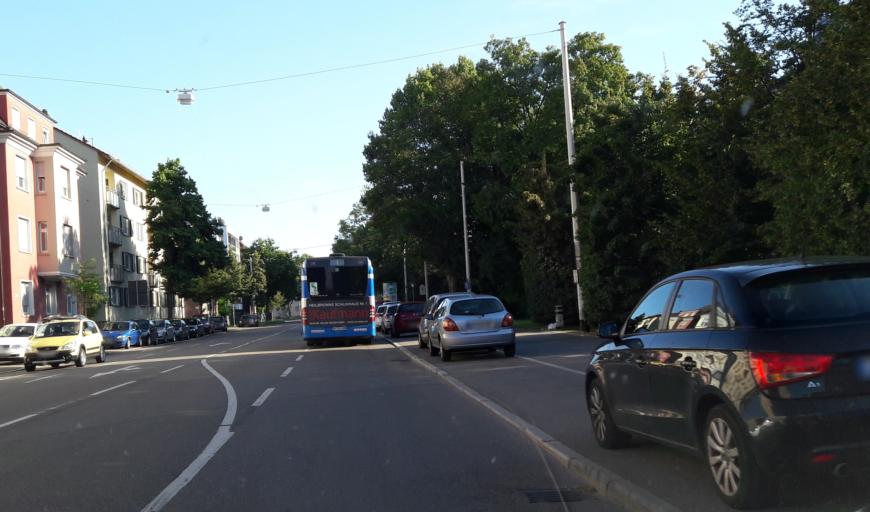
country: DE
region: Baden-Wuerttemberg
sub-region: Regierungsbezirk Stuttgart
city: Heilbronn
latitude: 49.1409
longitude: 9.2082
